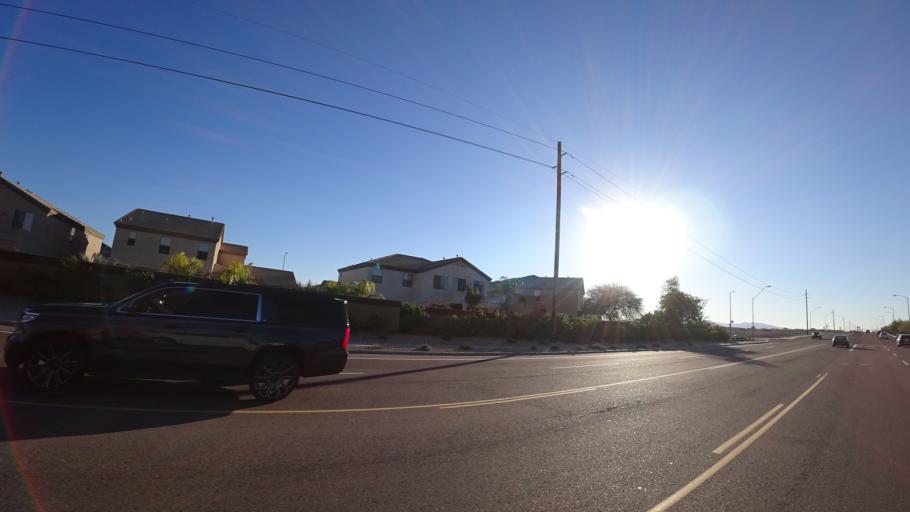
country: US
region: Arizona
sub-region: Maricopa County
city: Sun City West
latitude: 33.6818
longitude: -112.2625
